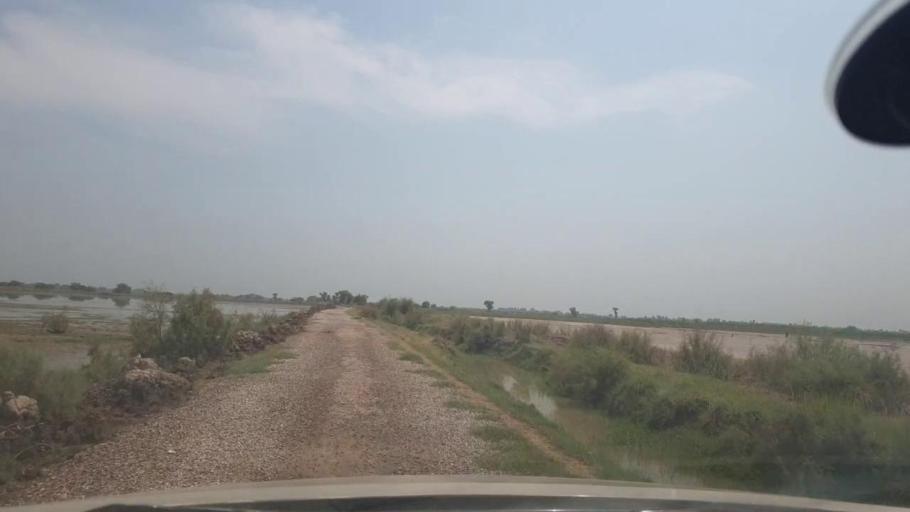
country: PK
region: Sindh
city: Jacobabad
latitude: 28.2295
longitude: 68.3932
